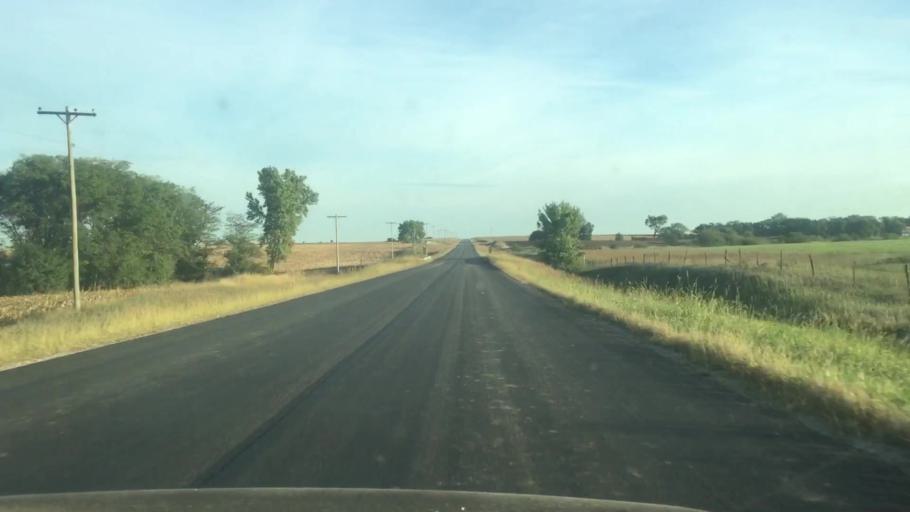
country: US
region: Kansas
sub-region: Marshall County
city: Marysville
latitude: 39.8806
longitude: -96.6010
